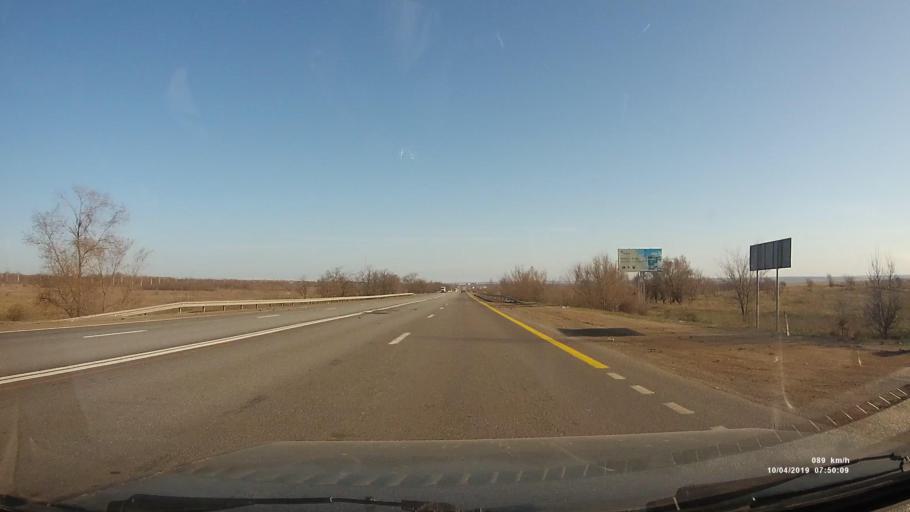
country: RU
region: Rostov
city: Kamensk-Shakhtinskiy
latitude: 48.2562
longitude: 40.2931
